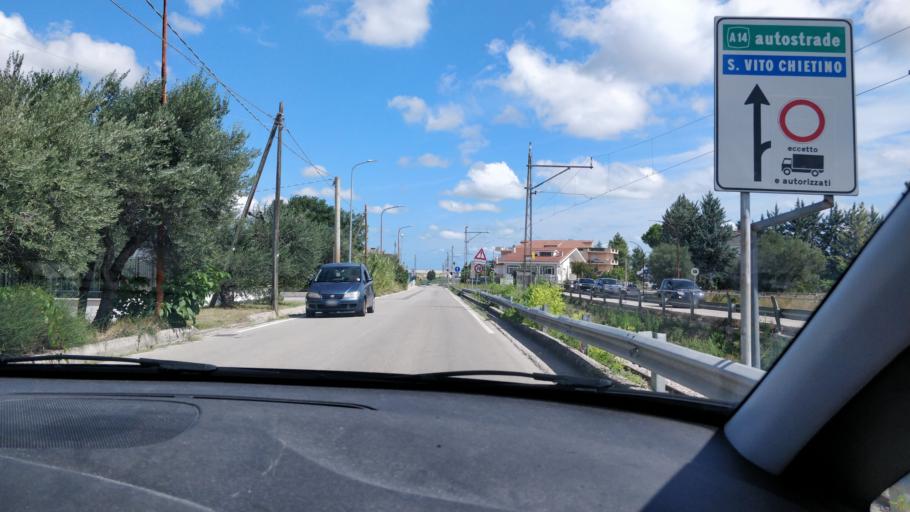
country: IT
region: Abruzzo
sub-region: Provincia di Chieti
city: Lanciano
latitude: 42.2335
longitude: 14.4058
